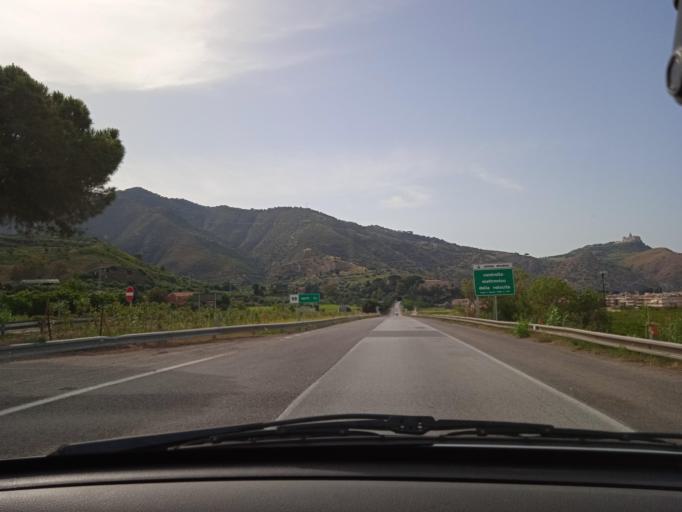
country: IT
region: Sicily
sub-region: Messina
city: Oliveri
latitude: 38.1160
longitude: 15.0644
